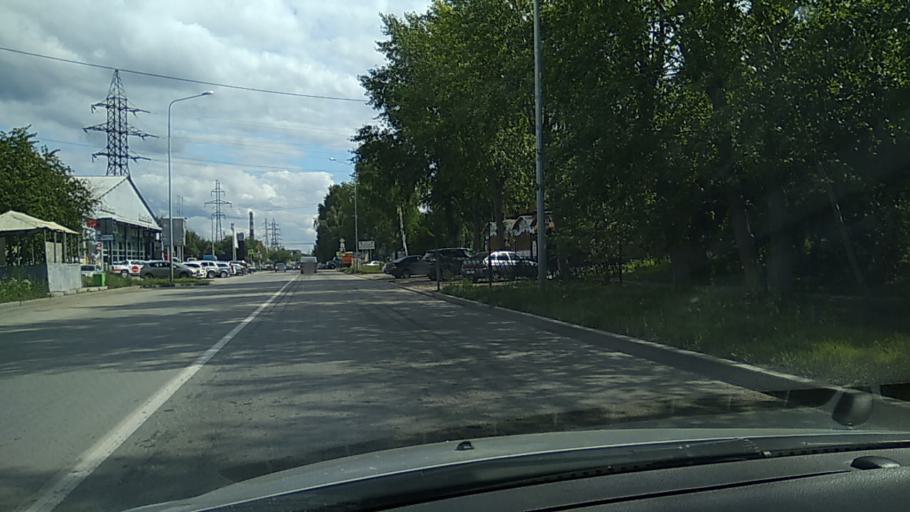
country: RU
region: Sverdlovsk
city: Shuvakish
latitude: 56.8855
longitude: 60.5310
